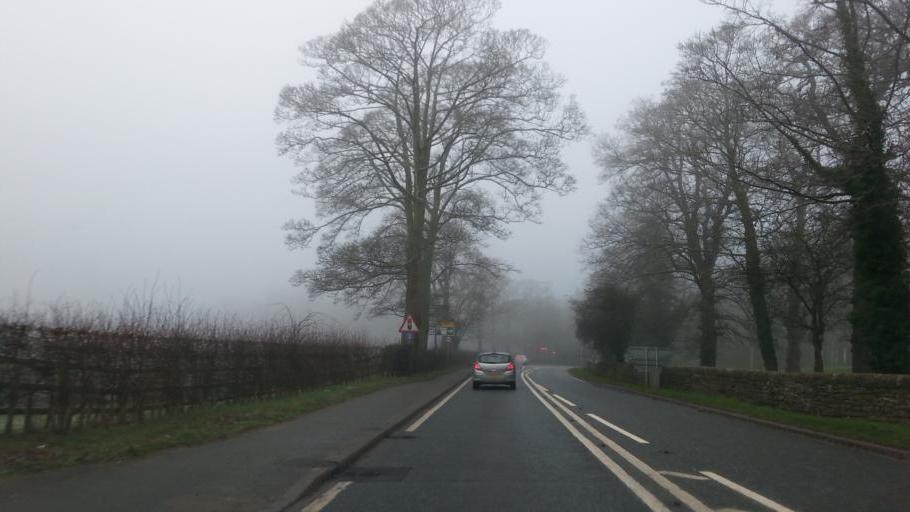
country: GB
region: England
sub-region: Cheshire East
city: Siddington
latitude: 53.2683
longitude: -2.2365
